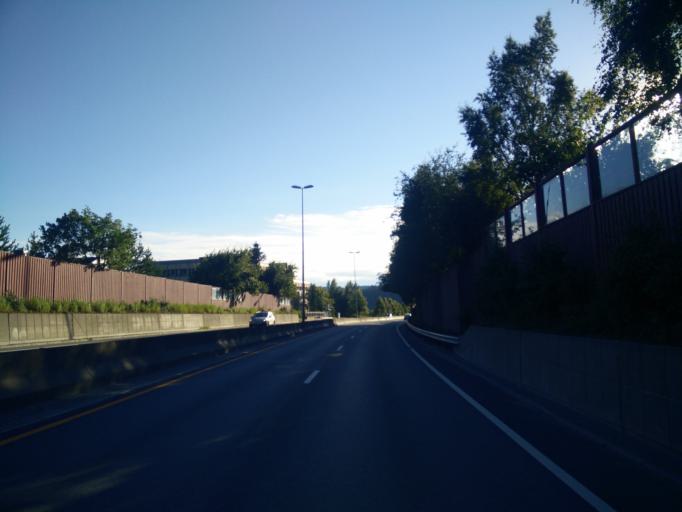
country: NO
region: Sor-Trondelag
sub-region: Trondheim
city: Trondheim
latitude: 63.4031
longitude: 10.4098
